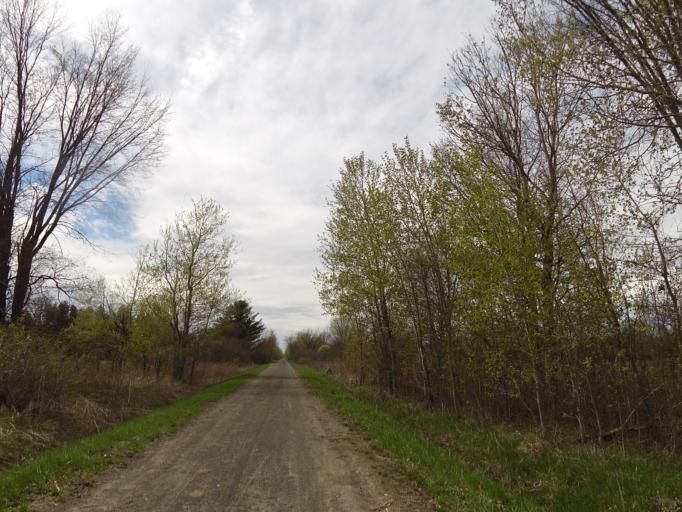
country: CA
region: Ontario
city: Hawkesbury
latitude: 45.5364
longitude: -74.7143
